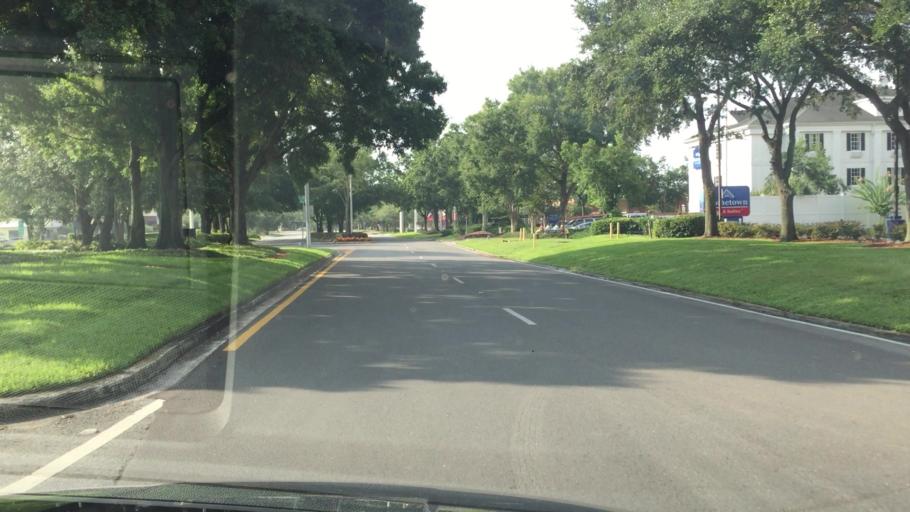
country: US
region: Florida
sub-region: Duval County
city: Jacksonville
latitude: 30.2473
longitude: -81.5990
